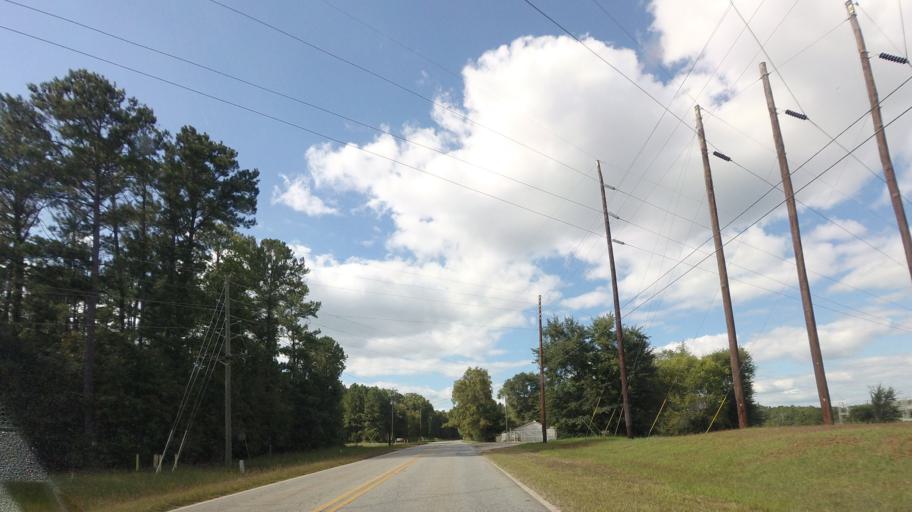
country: US
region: Georgia
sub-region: Bibb County
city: Macon
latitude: 32.9238
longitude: -83.7007
